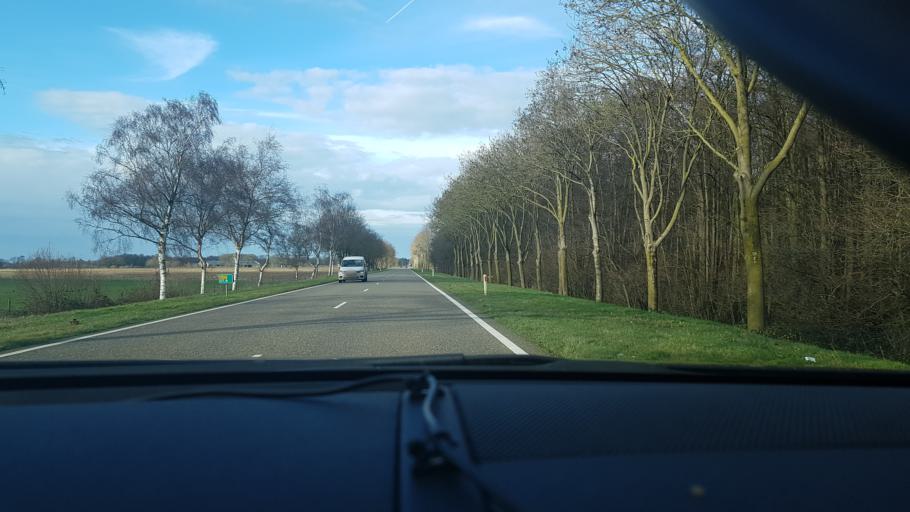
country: NL
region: Limburg
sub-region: Gemeente Peel en Maas
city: Maasbree
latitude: 51.3419
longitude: 6.0268
